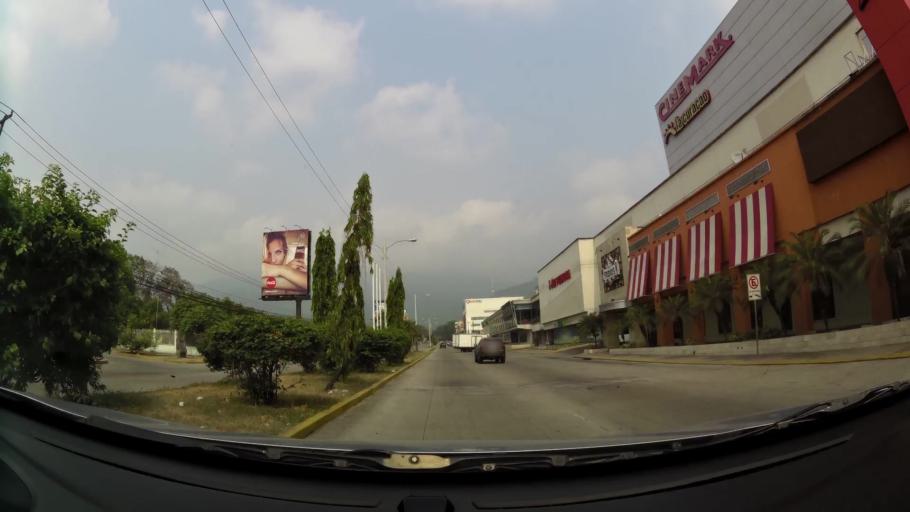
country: HN
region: Cortes
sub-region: San Pedro Sula
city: Pena Blanca
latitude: 15.5301
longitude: -88.0294
